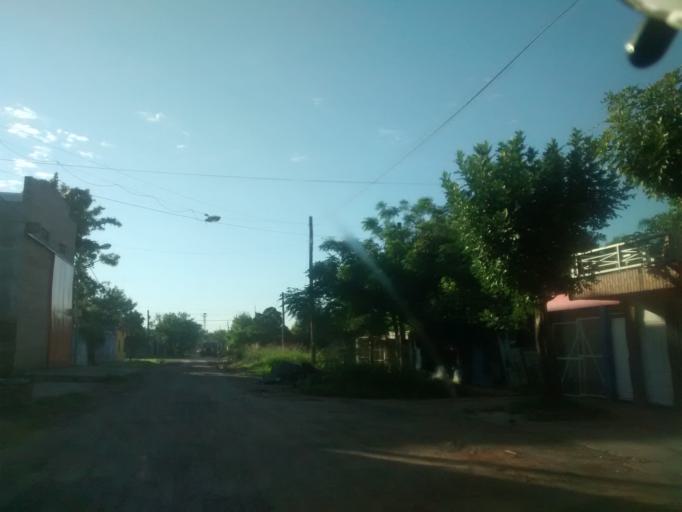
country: AR
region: Chaco
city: Resistencia
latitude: -27.4467
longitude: -59.0079
